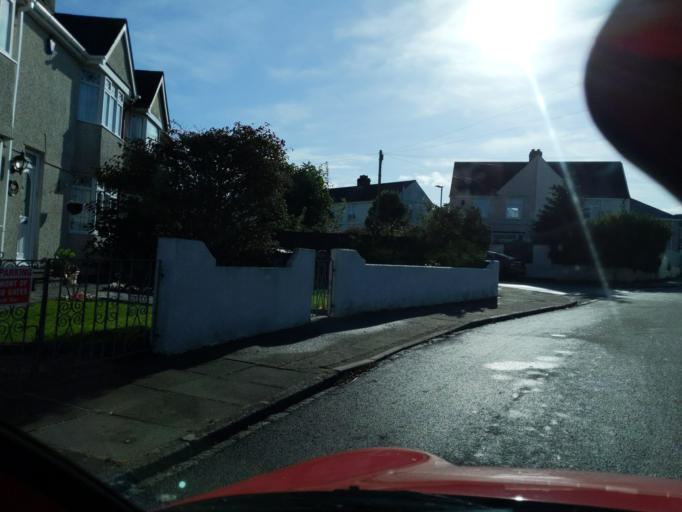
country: GB
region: England
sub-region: Cornwall
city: Torpoint
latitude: 50.4148
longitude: -4.1722
